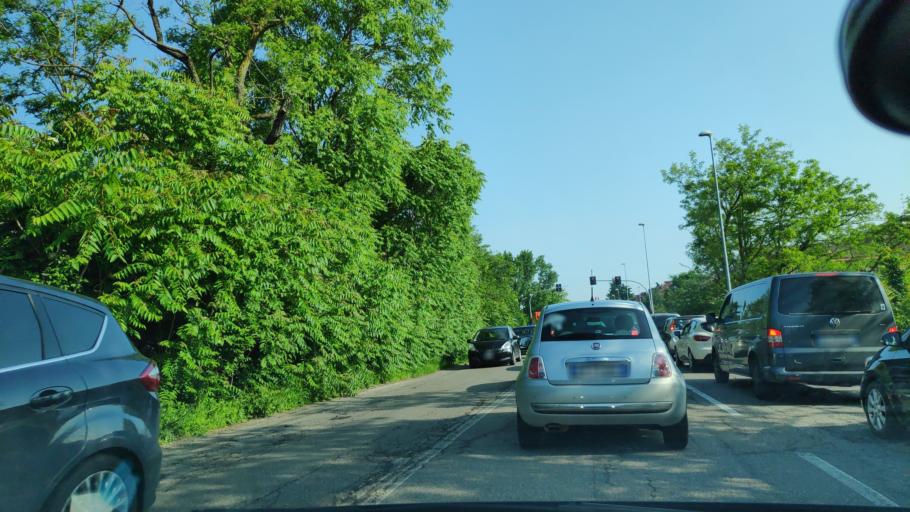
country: IT
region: Lombardy
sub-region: Citta metropolitana di Milano
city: Fizzonasco
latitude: 45.3663
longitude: 9.1896
